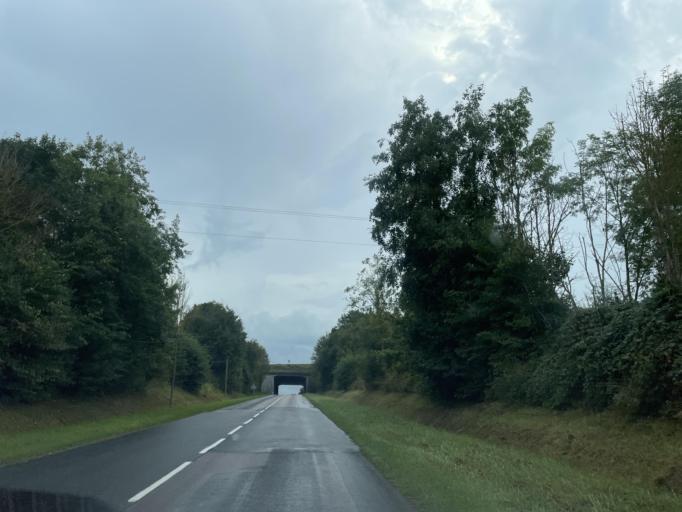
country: FR
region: Haute-Normandie
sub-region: Departement de la Seine-Maritime
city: Neufchatel-en-Bray
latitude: 49.7223
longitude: 1.4346
